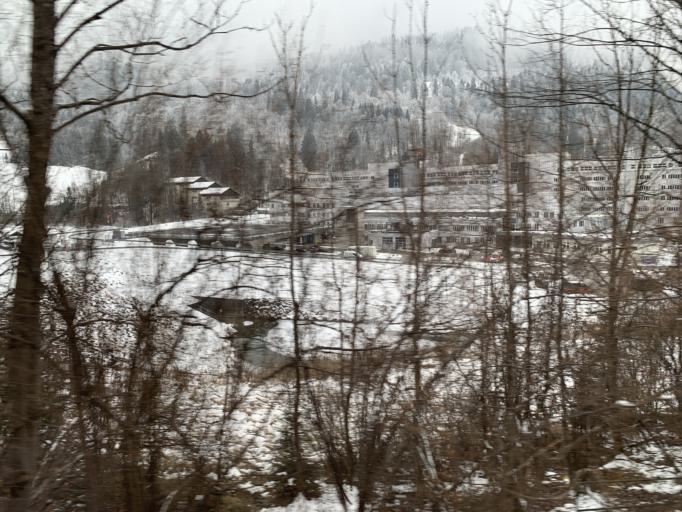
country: DE
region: Bavaria
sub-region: Upper Bavaria
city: Garmisch-Partenkirchen
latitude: 47.4855
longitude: 11.1284
